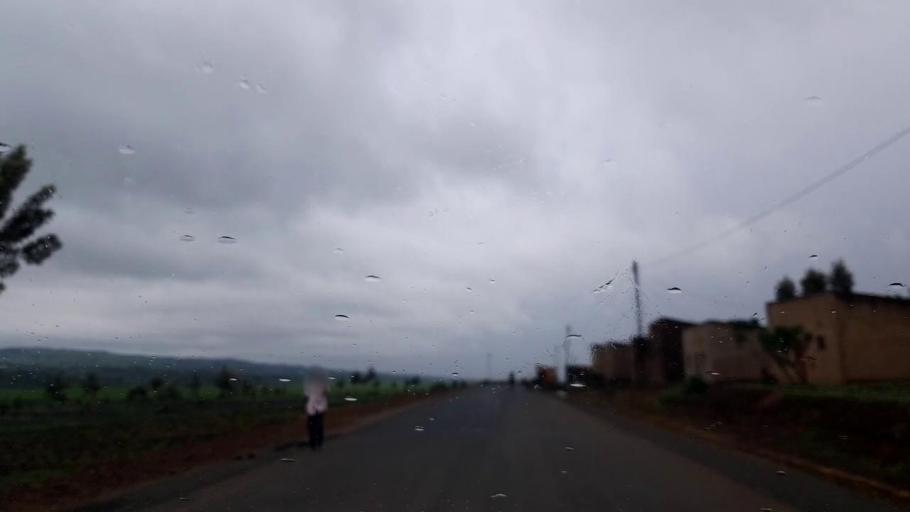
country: RW
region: Northern Province
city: Byumba
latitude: -1.4216
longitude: 30.2773
